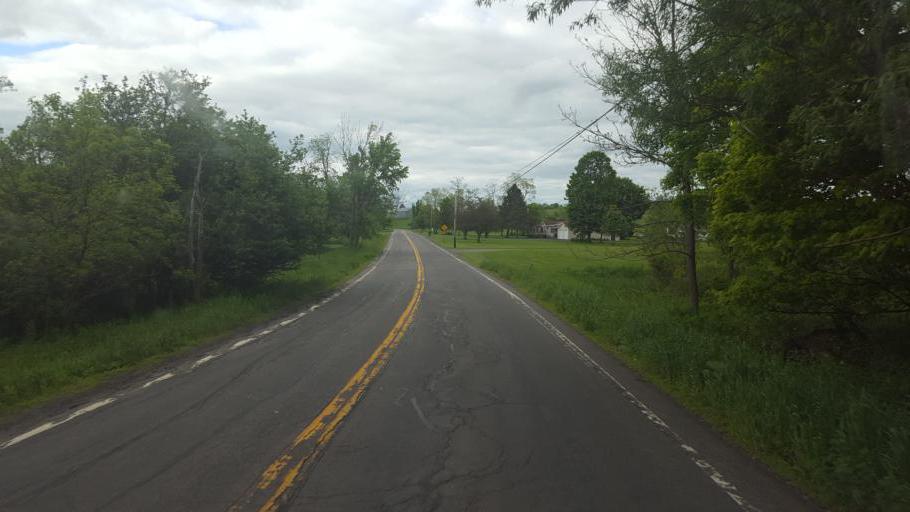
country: US
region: New York
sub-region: Otsego County
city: Richfield Springs
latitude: 42.8708
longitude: -74.9711
